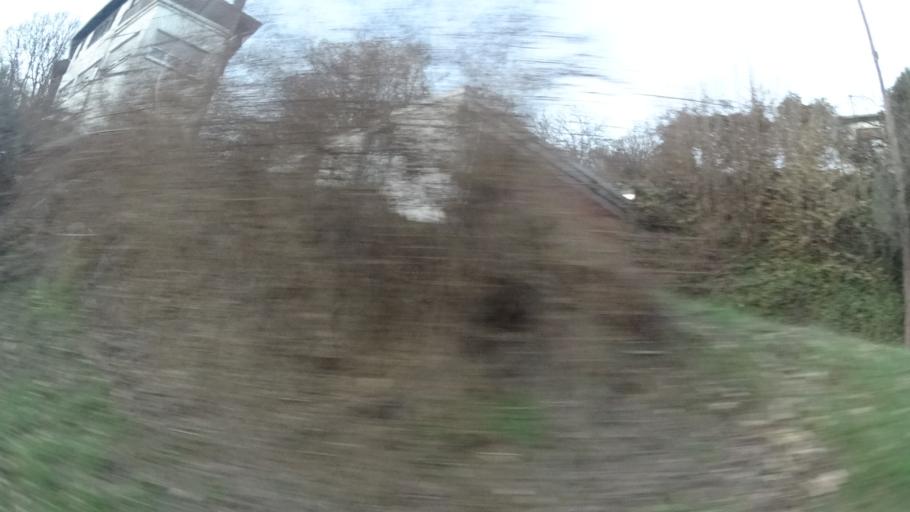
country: DE
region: Bavaria
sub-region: Regierungsbezirk Unterfranken
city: Mombris
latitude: 50.0861
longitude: 9.1528
